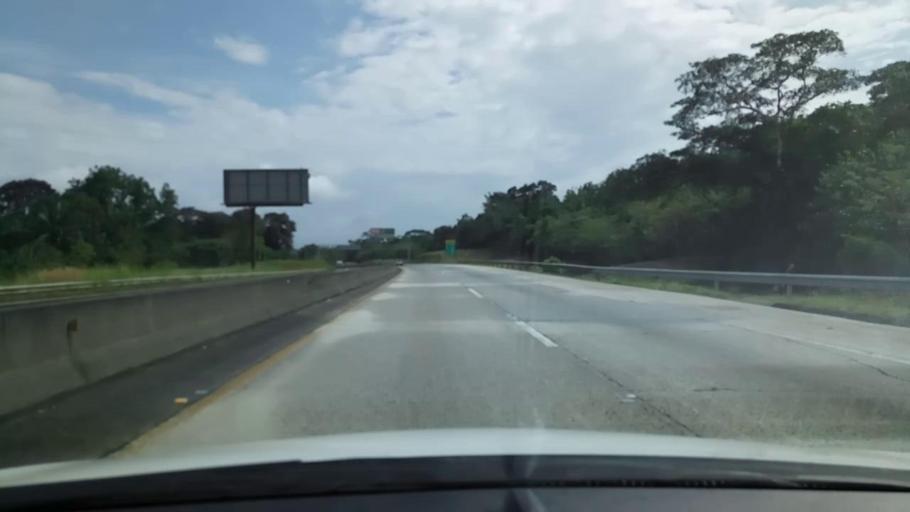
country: PA
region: Colon
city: Buena Vista
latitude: 9.2691
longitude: -79.7068
